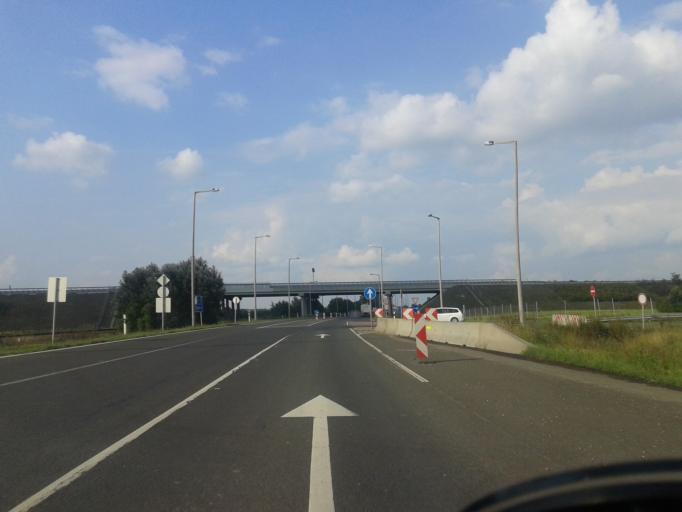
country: HU
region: Bacs-Kiskun
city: Dunavecse
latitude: 46.8951
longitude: 18.9836
